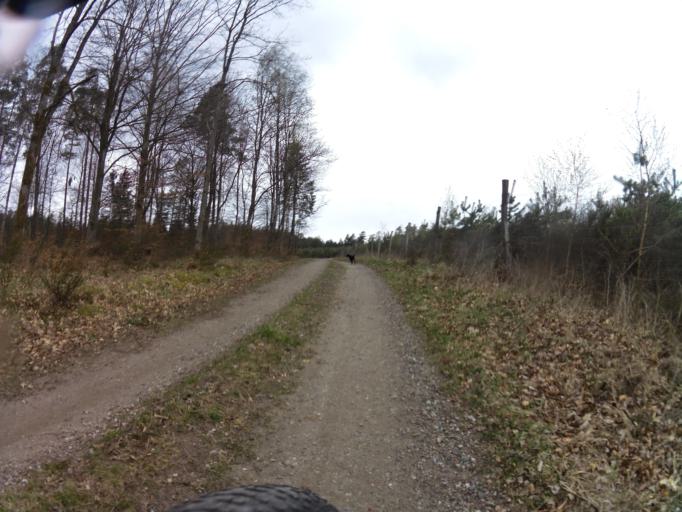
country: PL
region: West Pomeranian Voivodeship
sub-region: Powiat koszalinski
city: Polanow
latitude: 54.0688
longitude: 16.6238
